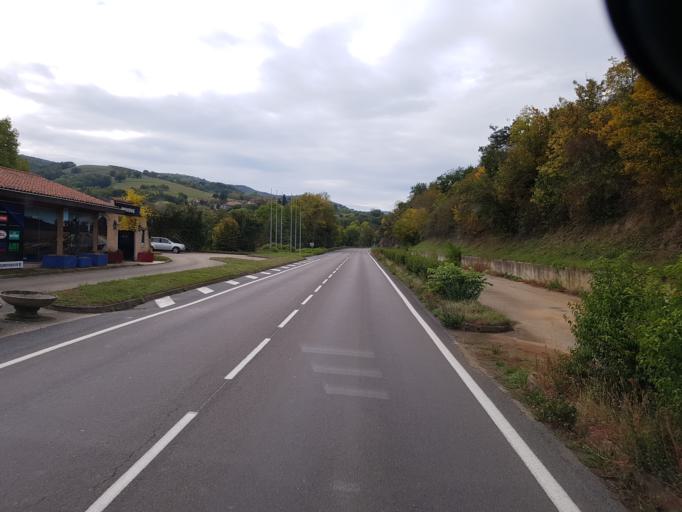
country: FR
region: Rhone-Alpes
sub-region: Departement du Rhone
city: Courzieu
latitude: 45.7488
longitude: 4.5430
